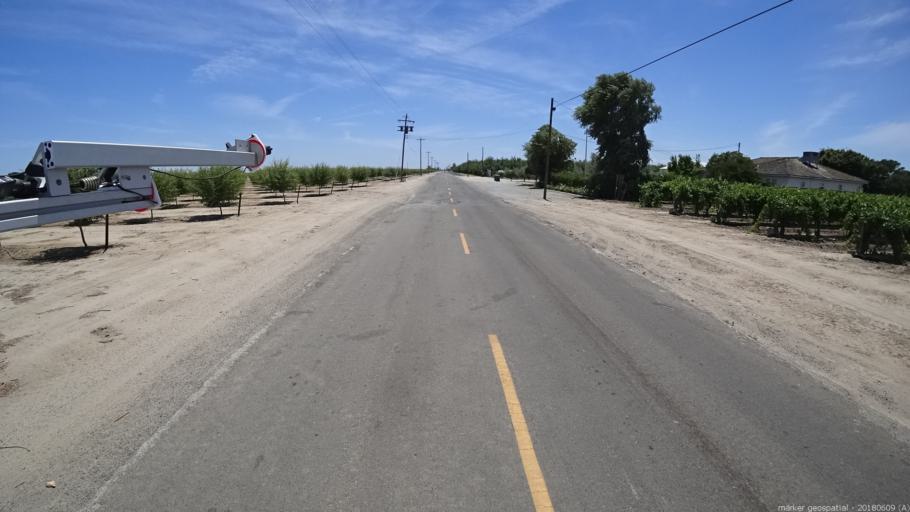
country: US
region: California
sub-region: Madera County
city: Parkwood
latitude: 36.8559
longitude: -120.0922
